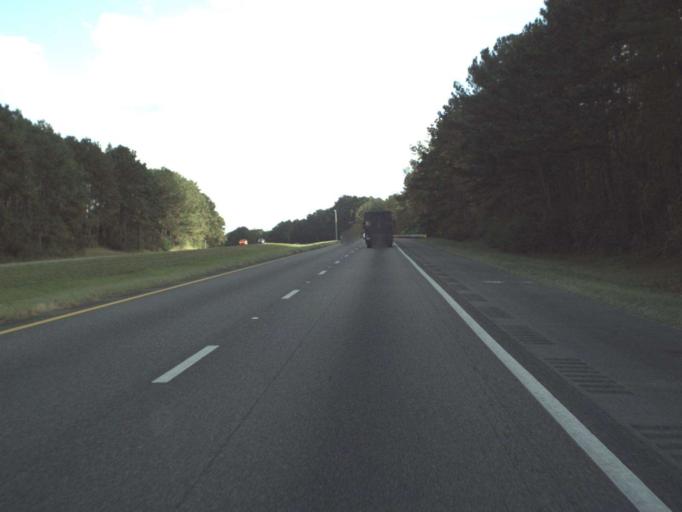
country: US
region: Florida
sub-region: Gadsden County
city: Quincy
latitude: 30.5316
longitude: -84.5729
